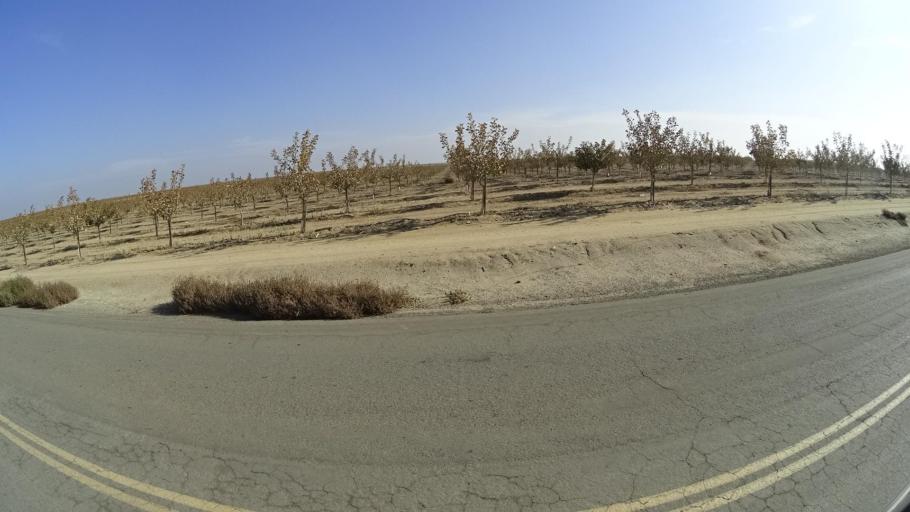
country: US
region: California
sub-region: Kern County
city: McFarland
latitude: 35.6185
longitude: -119.1688
